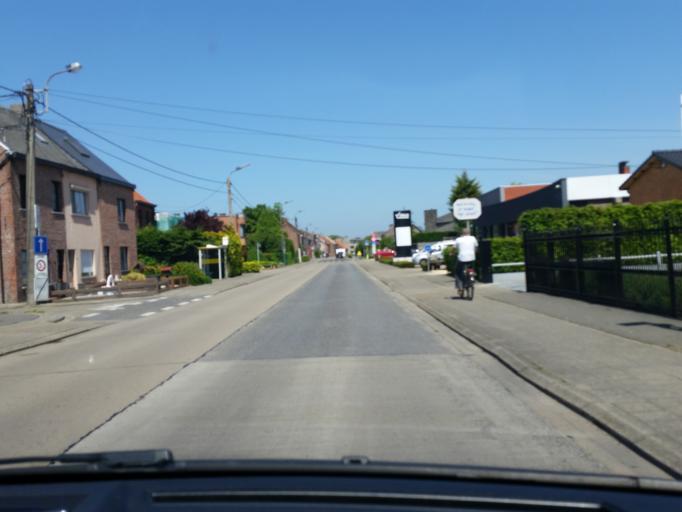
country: BE
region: Flanders
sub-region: Provincie Antwerpen
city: Mechelen
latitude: 51.0452
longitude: 4.5028
